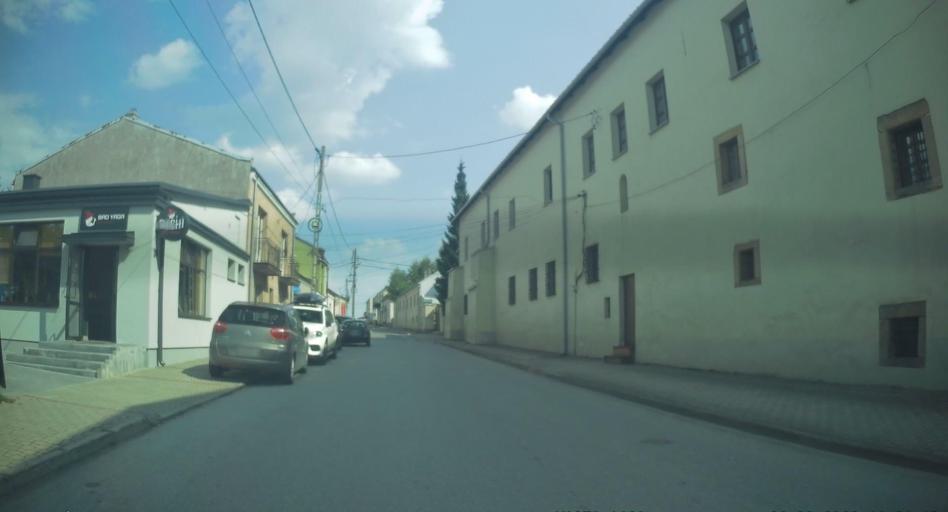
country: PL
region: Swietokrzyskie
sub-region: Powiat kielecki
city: Checiny
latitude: 50.8012
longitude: 20.4592
